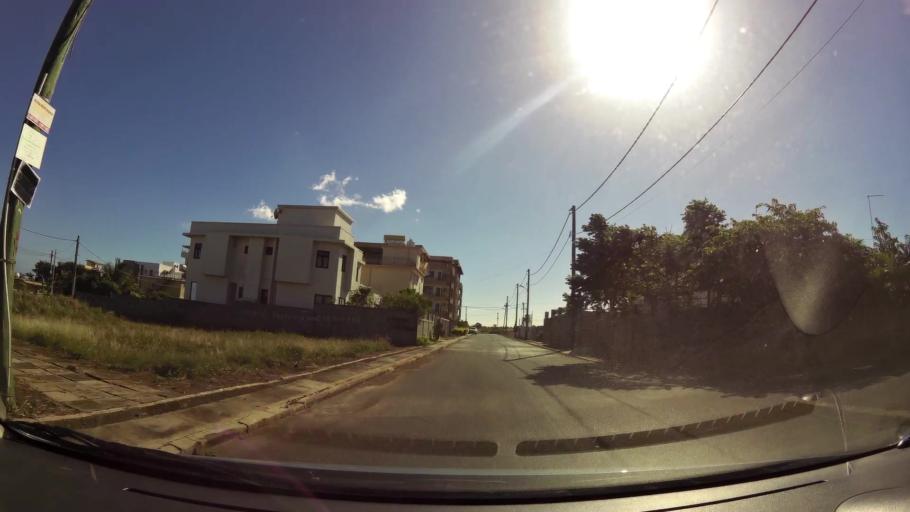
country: MU
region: Black River
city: Flic en Flac
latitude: -20.2778
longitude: 57.3789
